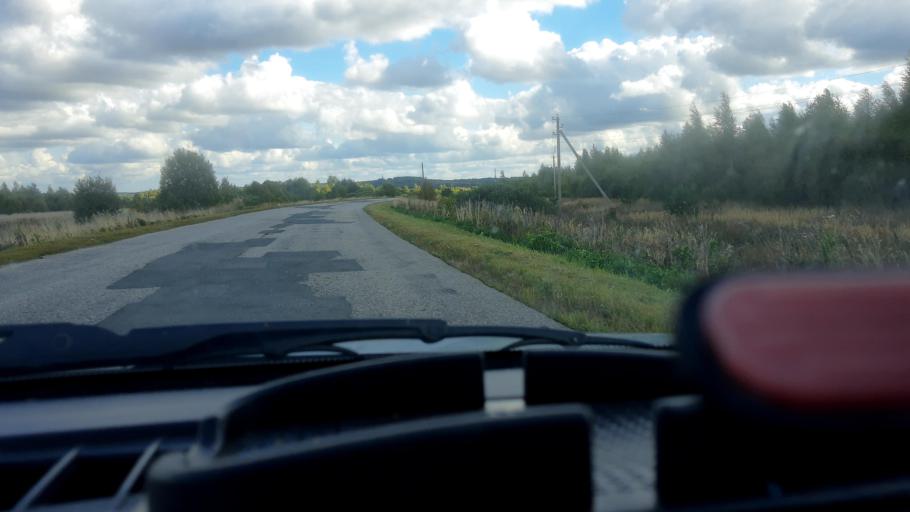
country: RU
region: Mariy-El
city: Kilemary
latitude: 56.9421
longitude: 46.6801
